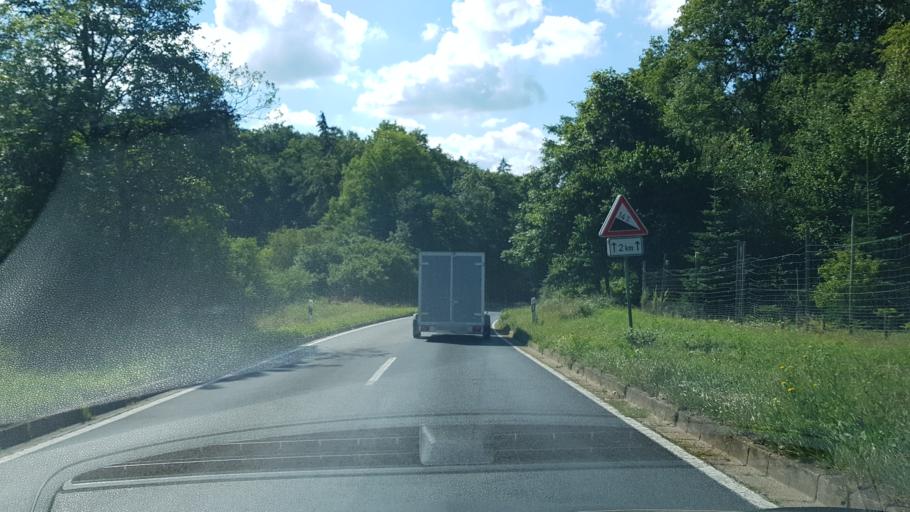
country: DE
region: Rheinland-Pfalz
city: Ernst
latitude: 50.1472
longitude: 7.2568
